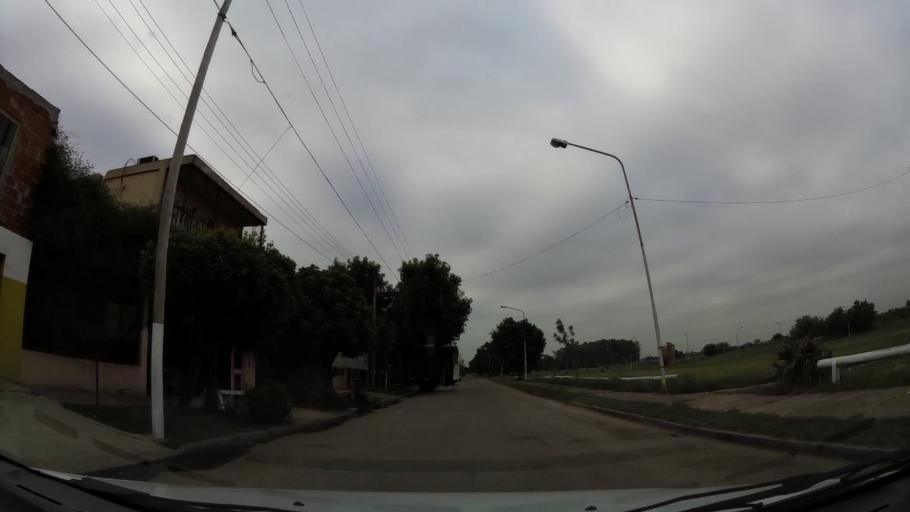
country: AR
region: Buenos Aires
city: San Justo
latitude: -34.7031
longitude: -58.5550
